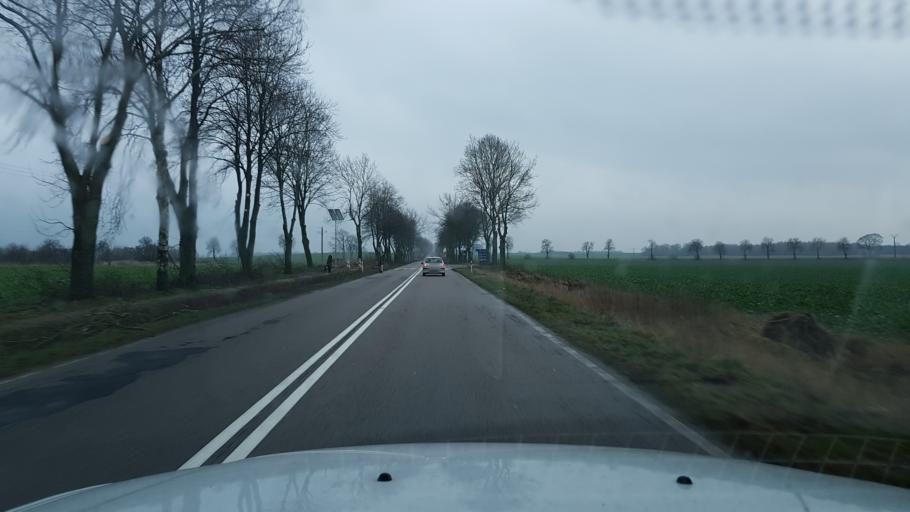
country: PL
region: West Pomeranian Voivodeship
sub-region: Powiat gryficki
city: Ploty
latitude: 53.8450
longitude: 15.2335
